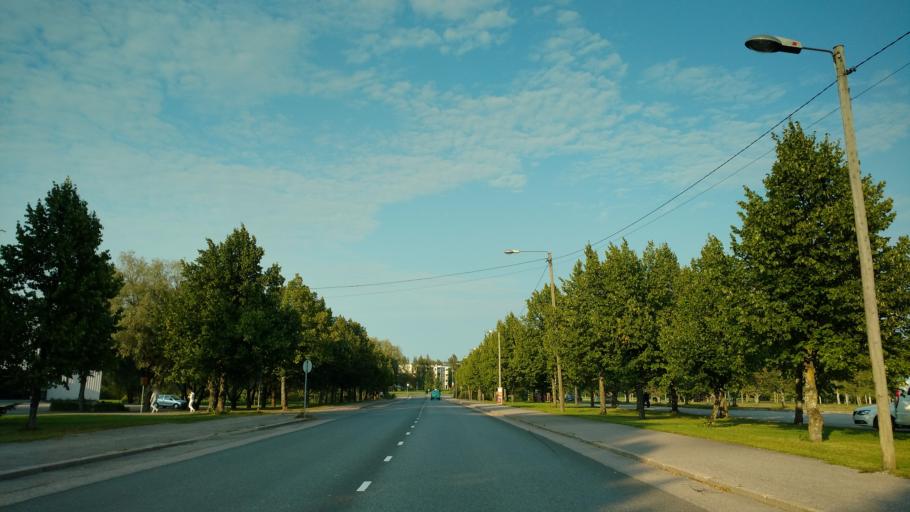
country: FI
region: Varsinais-Suomi
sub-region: Salo
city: Salo
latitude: 60.3828
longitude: 23.1407
